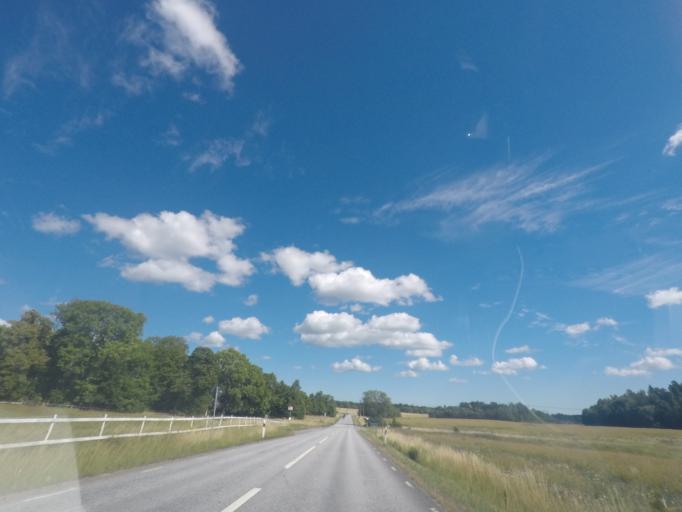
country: SE
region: Stockholm
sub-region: Norrtalje Kommun
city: Hallstavik
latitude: 59.9336
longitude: 18.7154
